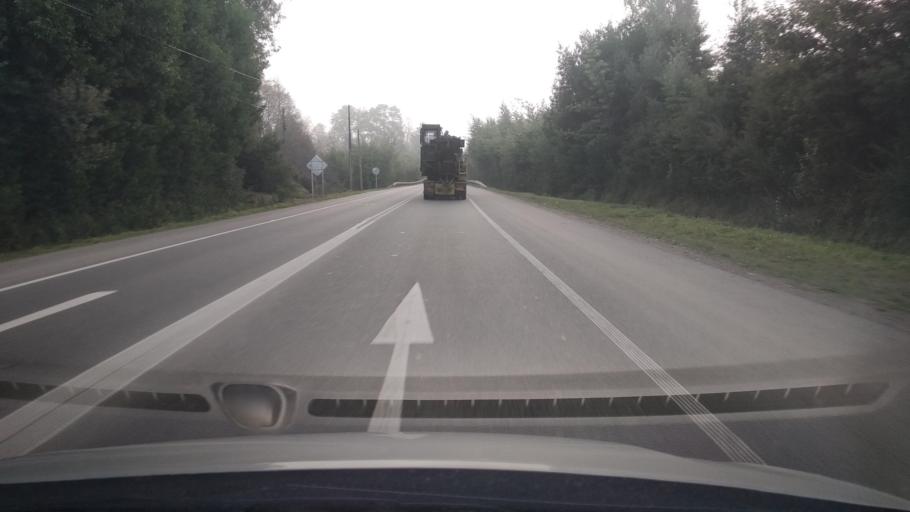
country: CL
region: Los Lagos
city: Las Animas
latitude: -39.7694
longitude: -73.2226
